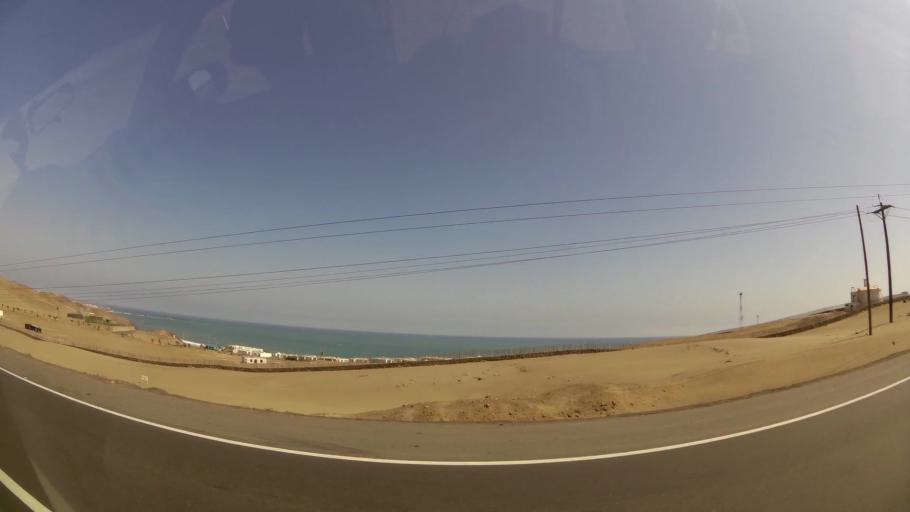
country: PE
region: Lima
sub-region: Provincia de Canete
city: Quilmana
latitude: -12.9222
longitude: -76.5007
